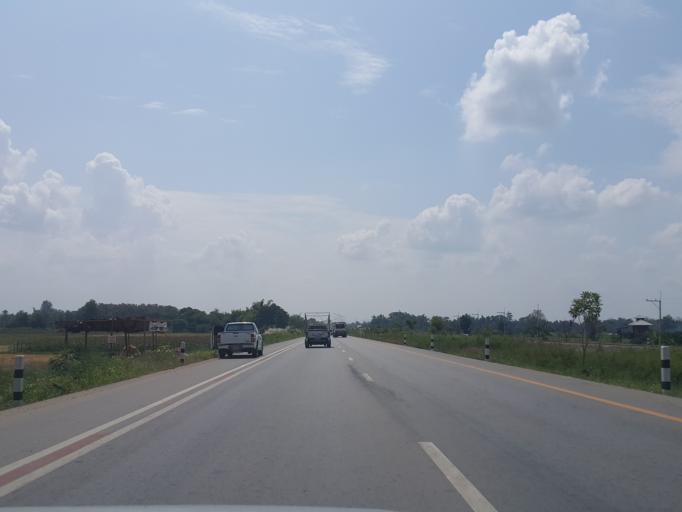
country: TH
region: Chiang Mai
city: San Pa Tong
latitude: 18.6288
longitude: 98.8391
